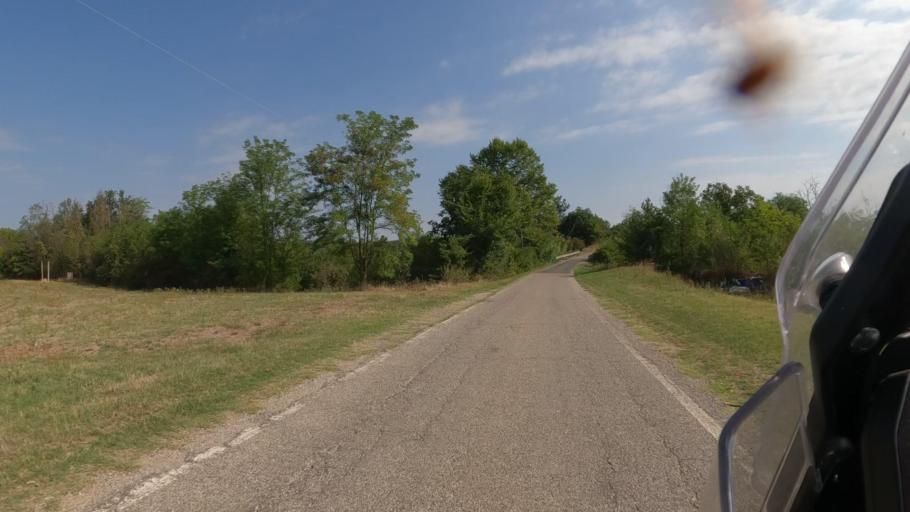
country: IT
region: Piedmont
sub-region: Provincia di Alessandria
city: Altavilla Monferrato
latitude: 44.9648
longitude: 8.3824
